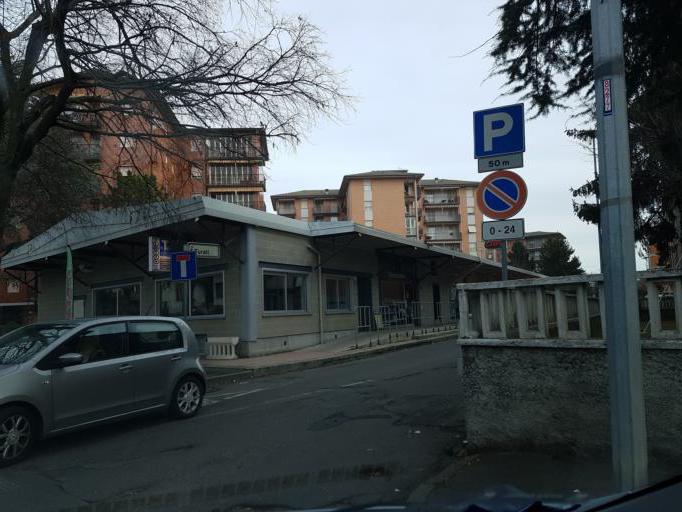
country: IT
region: Piedmont
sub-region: Provincia di Alessandria
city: Novi Ligure
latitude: 44.7675
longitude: 8.7981
